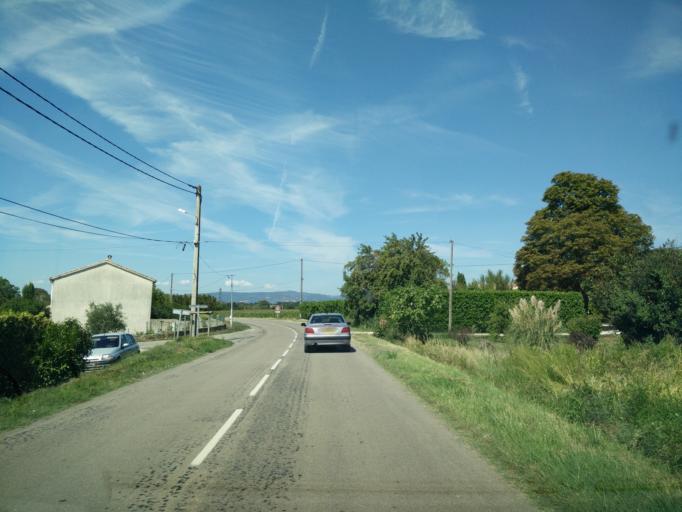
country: FR
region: Rhone-Alpes
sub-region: Departement de la Drome
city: Montboucher-sur-Jabron
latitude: 44.5483
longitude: 4.8405
